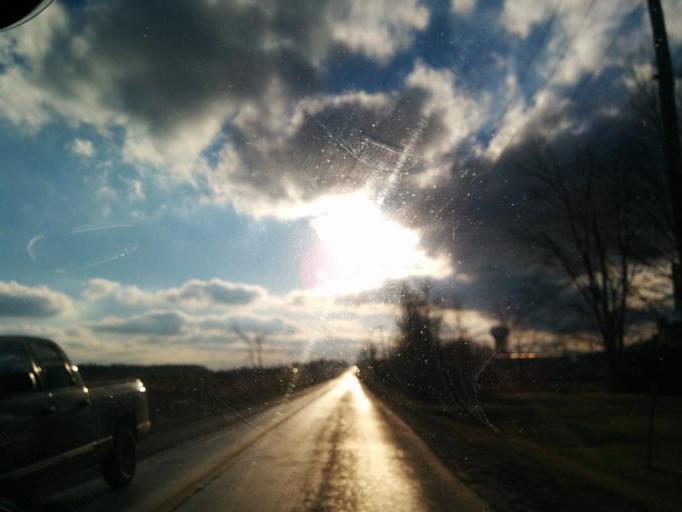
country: CA
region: Ontario
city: Oakville
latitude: 43.5064
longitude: -79.7331
